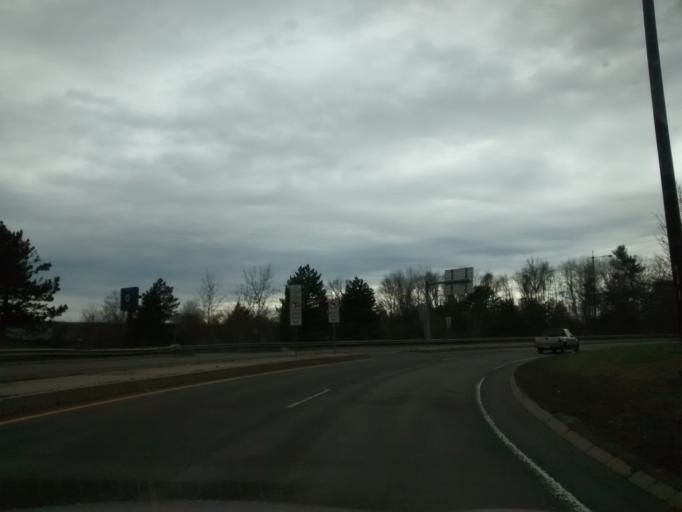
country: US
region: Massachusetts
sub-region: Worcester County
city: Millbury
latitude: 42.2096
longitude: -71.7873
